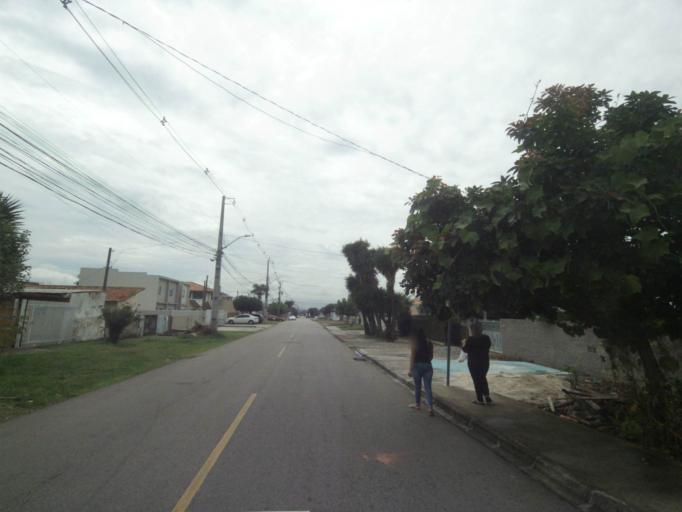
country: BR
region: Parana
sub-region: Pinhais
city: Pinhais
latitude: -25.4685
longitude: -49.1968
